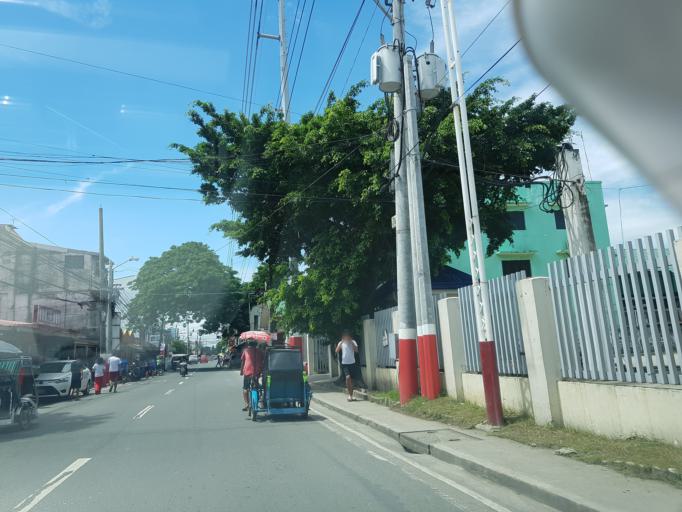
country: PH
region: Calabarzon
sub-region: Province of Rizal
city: Taguig
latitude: 14.5058
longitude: 121.0655
